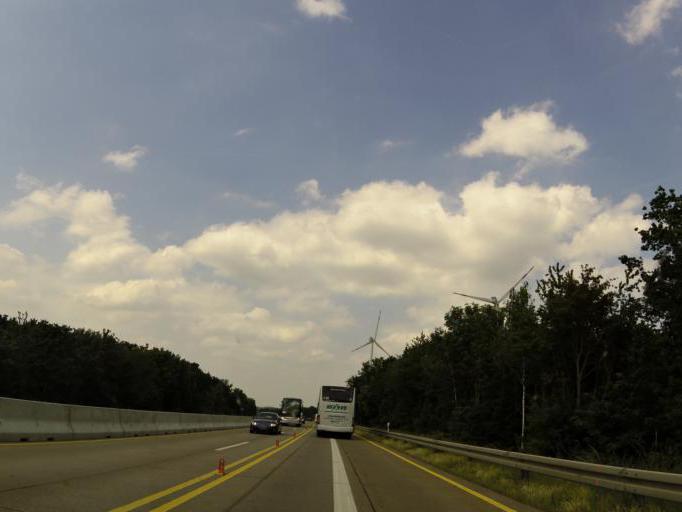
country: DE
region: Bavaria
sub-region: Regierungsbezirk Mittelfranken
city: Gollhofen
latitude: 49.5265
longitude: 10.1922
